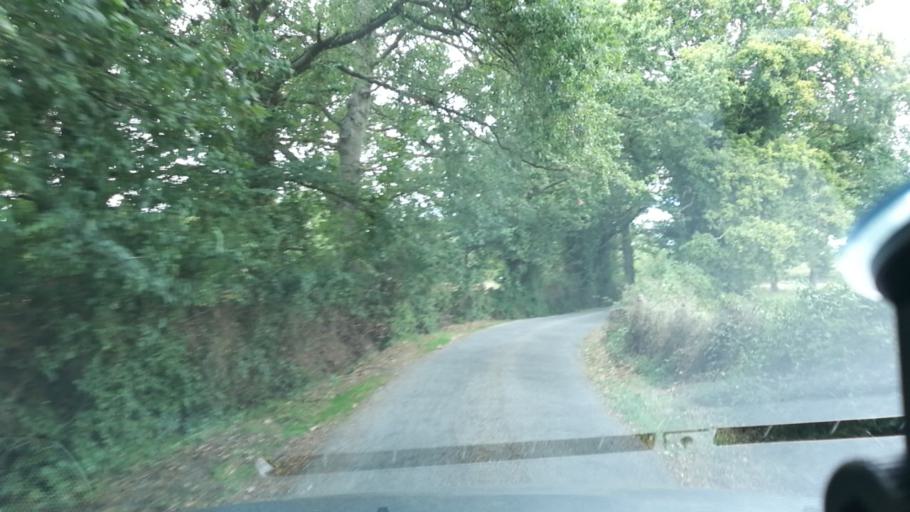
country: FR
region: Brittany
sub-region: Departement d'Ille-et-Vilaine
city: Saint-Jacques-de-la-Lande
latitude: 48.0895
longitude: -1.7295
